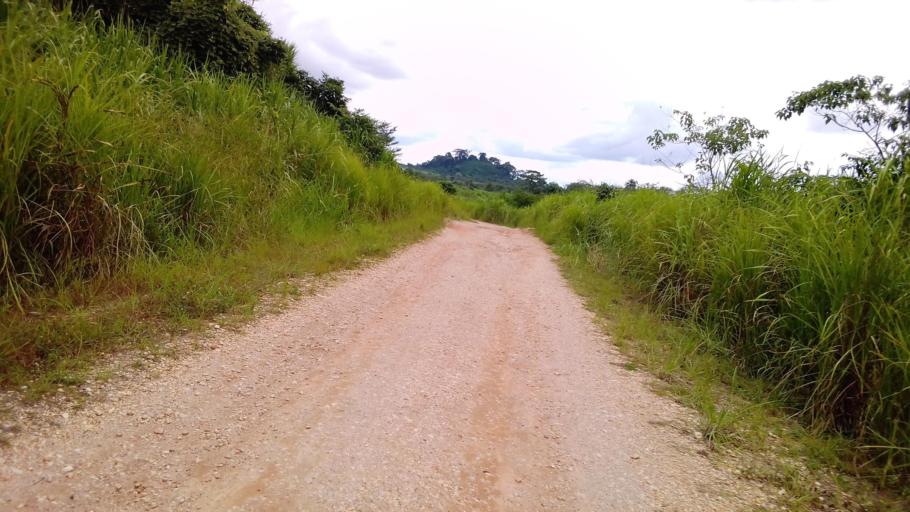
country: SL
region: Eastern Province
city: Koidu
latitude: 8.6809
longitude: -10.9641
